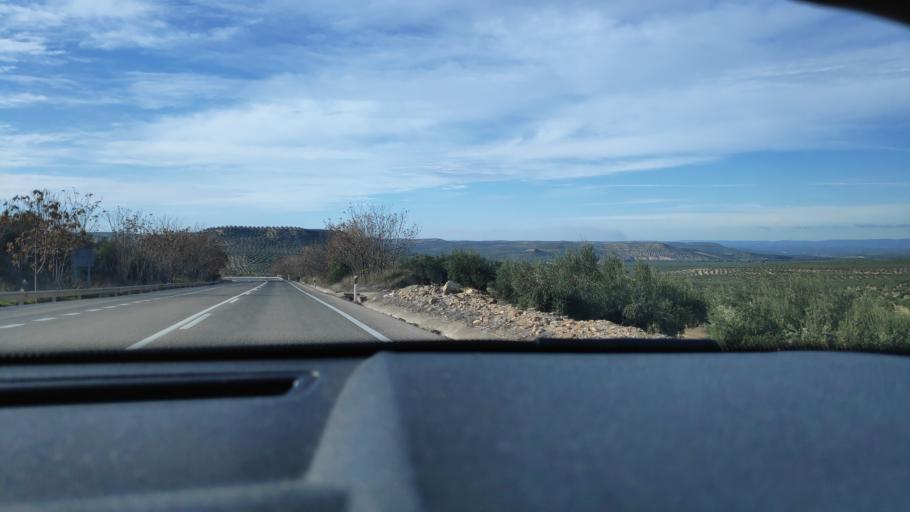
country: ES
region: Andalusia
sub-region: Provincia de Jaen
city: Porcuna
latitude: 37.8799
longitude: -4.1971
